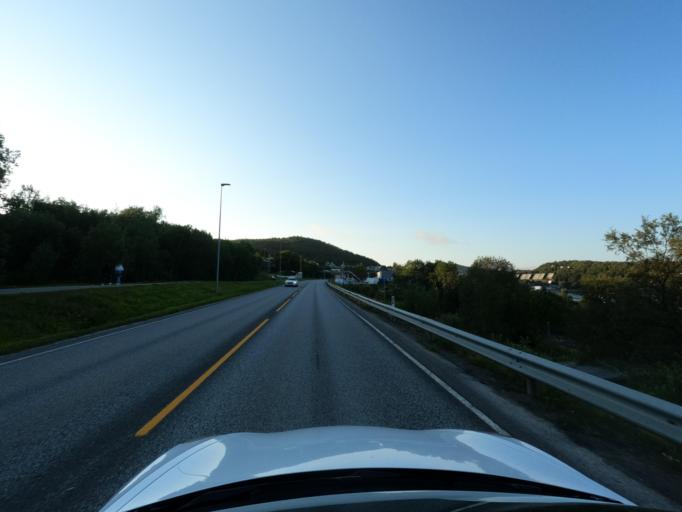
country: NO
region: Troms
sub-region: Harstad
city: Harstad
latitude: 68.7689
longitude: 16.5583
